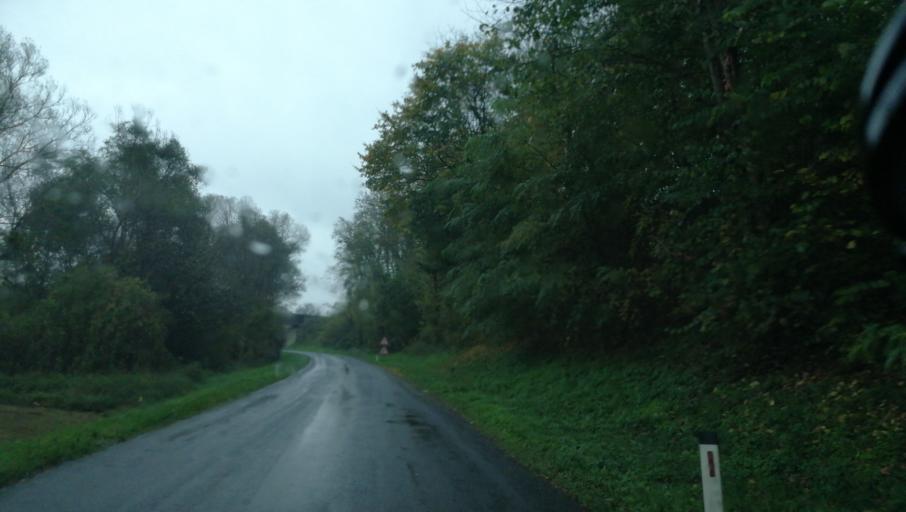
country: AT
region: Styria
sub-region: Politischer Bezirk Leibnitz
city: Spielfeld
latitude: 46.7120
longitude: 15.6257
